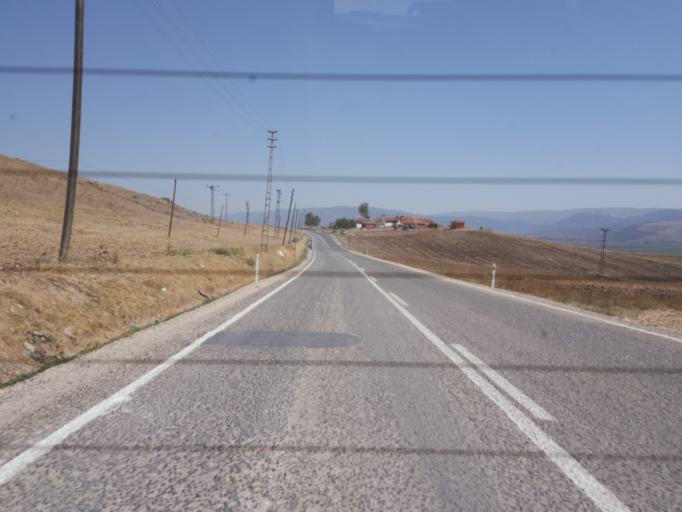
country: TR
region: Amasya
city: Dogantepe
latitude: 40.5833
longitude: 35.6287
